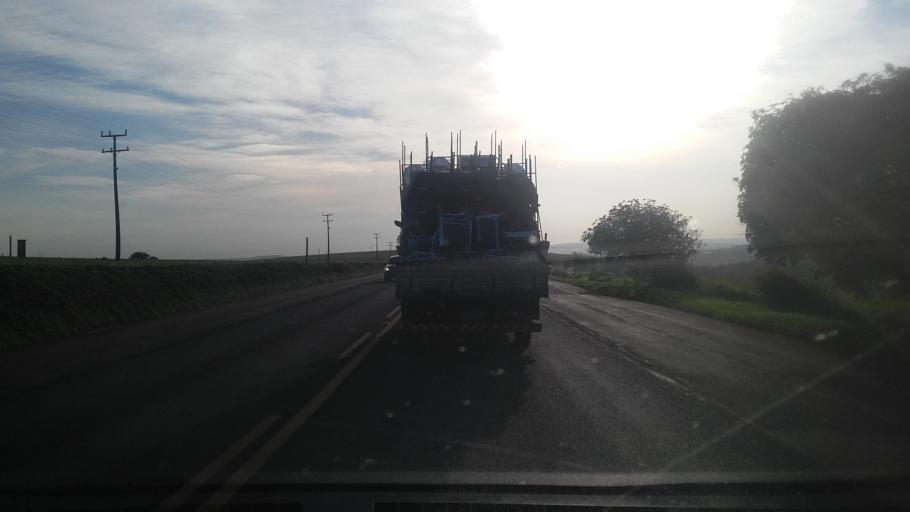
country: BR
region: Parana
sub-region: Bandeirantes
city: Bandeirantes
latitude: -23.1472
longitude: -50.5554
